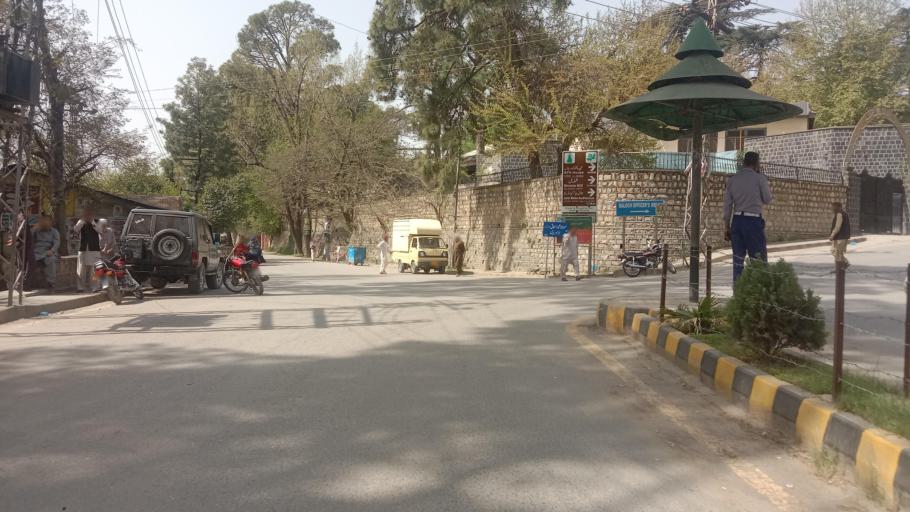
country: PK
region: Khyber Pakhtunkhwa
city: Abbottabad
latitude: 34.1434
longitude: 73.2106
